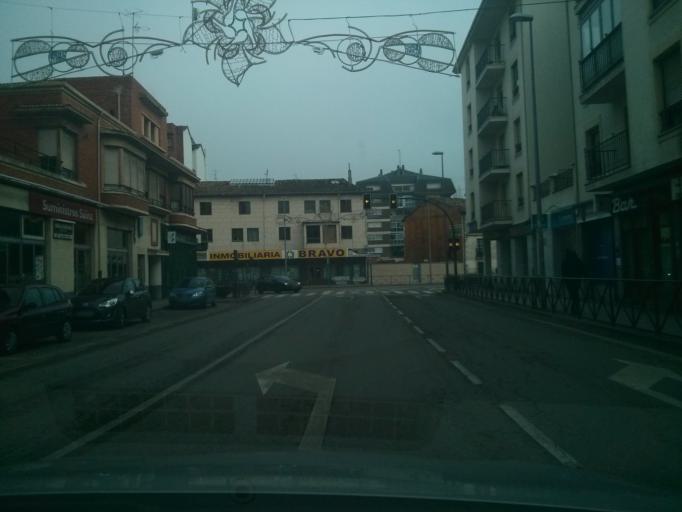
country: ES
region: Castille and Leon
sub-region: Provincia de Burgos
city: Medina de Pomar
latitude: 42.9323
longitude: -3.4867
